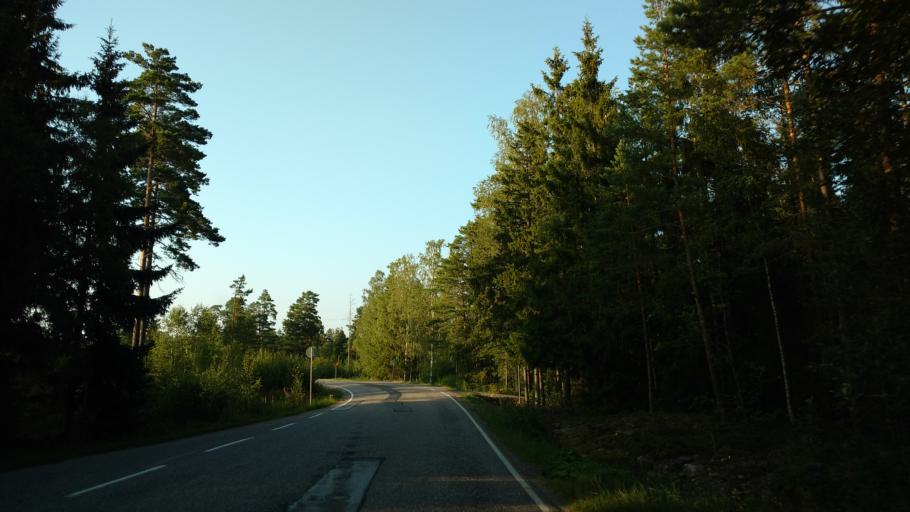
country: FI
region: Varsinais-Suomi
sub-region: Aboland-Turunmaa
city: Dragsfjaerd
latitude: 60.0270
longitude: 22.4607
